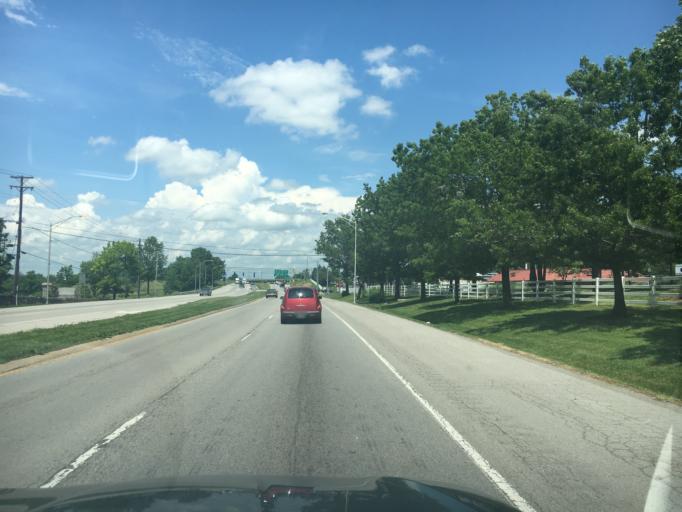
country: US
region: Kentucky
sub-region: Fayette County
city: Lexington-Fayette
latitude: 38.0939
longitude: -84.4868
